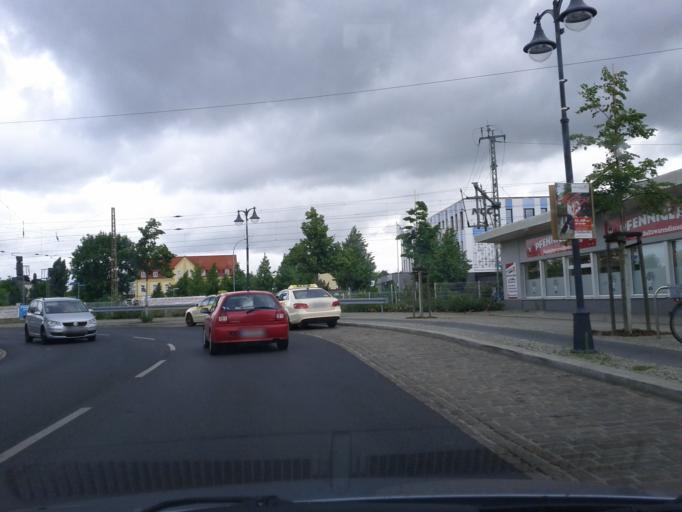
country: DE
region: Brandenburg
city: Furstenwalde
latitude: 52.3660
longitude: 14.0612
